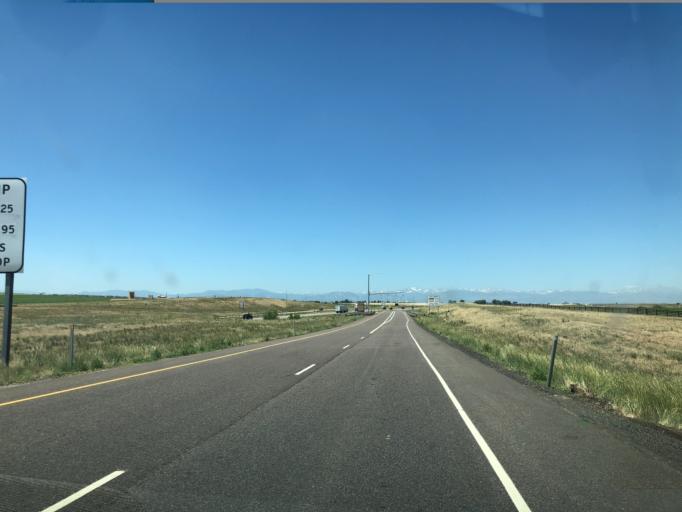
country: US
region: Colorado
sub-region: Adams County
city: Todd Creek
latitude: 39.9621
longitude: -104.9042
